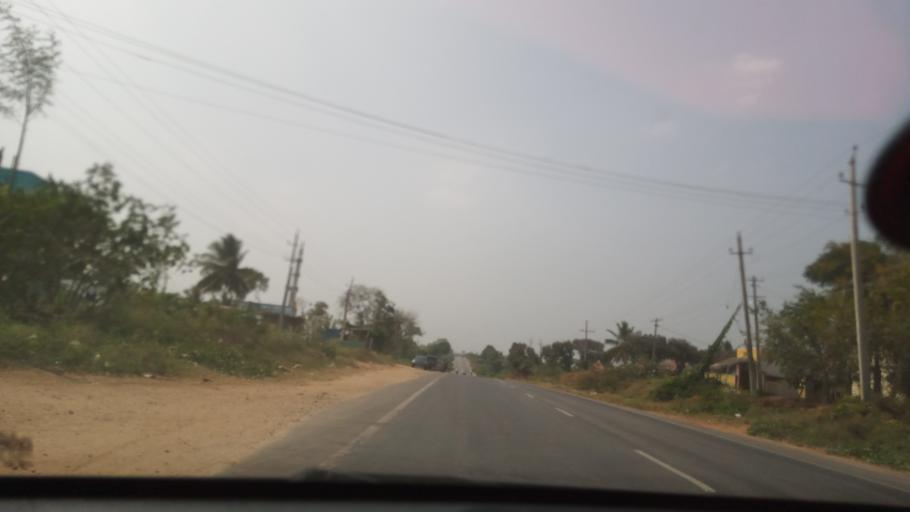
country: IN
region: Karnataka
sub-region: Chamrajnagar
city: Chamrajnagar
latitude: 11.9975
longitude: 76.8496
